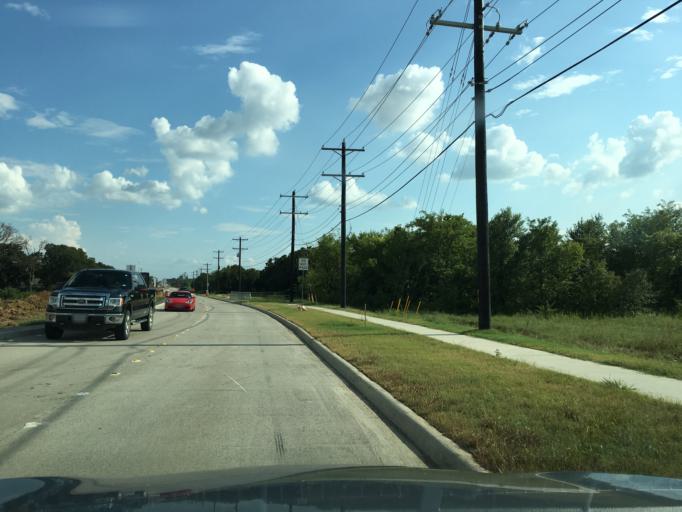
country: US
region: Texas
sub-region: Denton County
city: Denton
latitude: 33.2322
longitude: -97.0827
